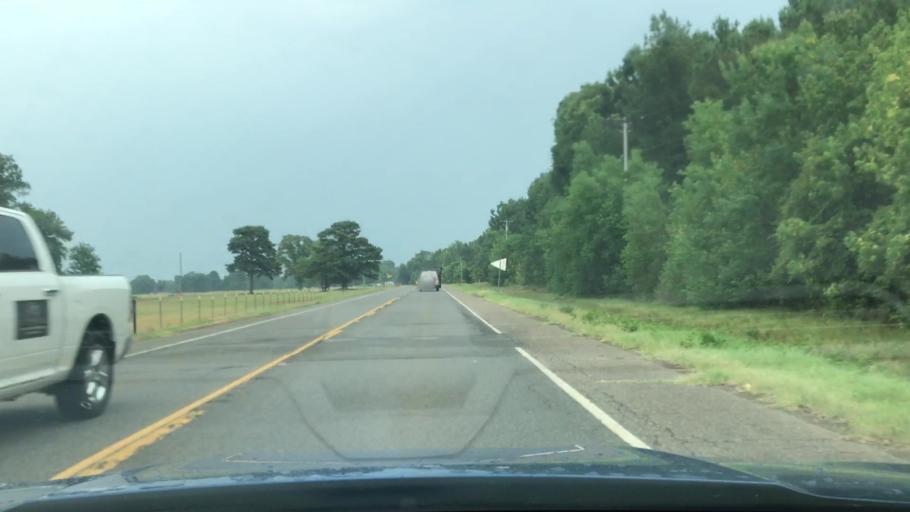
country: US
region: Texas
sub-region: Harrison County
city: Waskom
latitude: 32.4642
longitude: -94.0329
